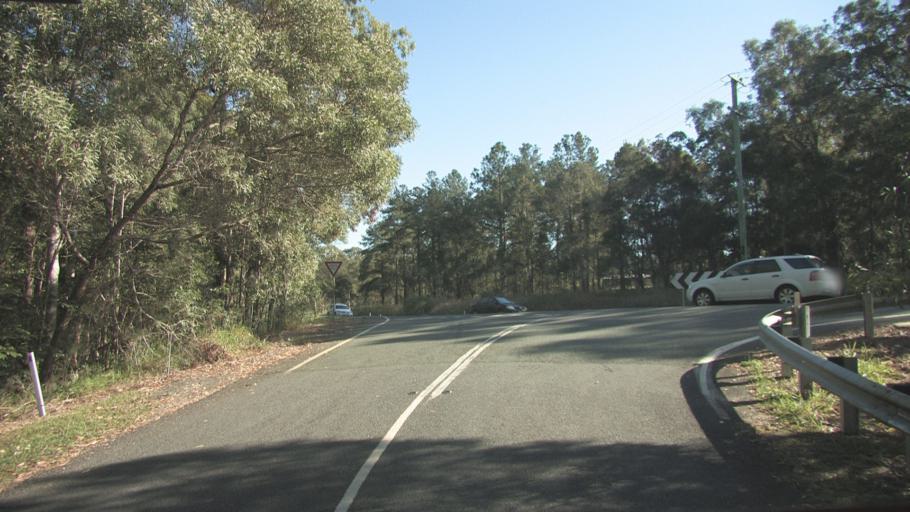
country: AU
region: Queensland
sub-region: Gold Coast
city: Yatala
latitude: -27.6885
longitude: 153.2781
